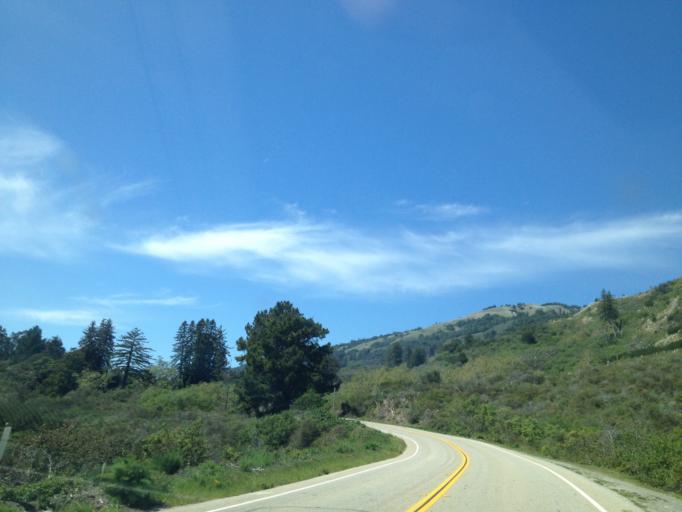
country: US
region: California
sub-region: Monterey County
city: Greenfield
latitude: 36.0177
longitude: -121.5354
